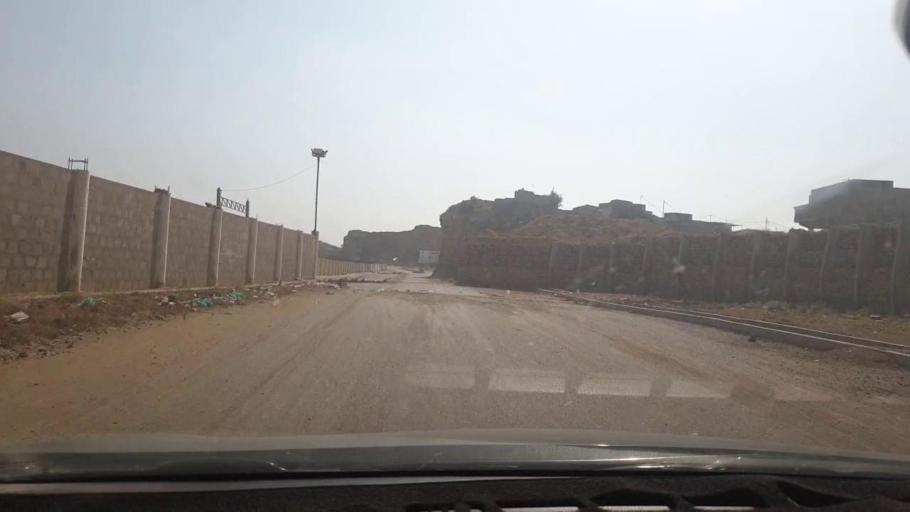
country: PK
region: Sindh
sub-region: Karachi District
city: Karachi
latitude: 24.9699
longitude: 66.9979
